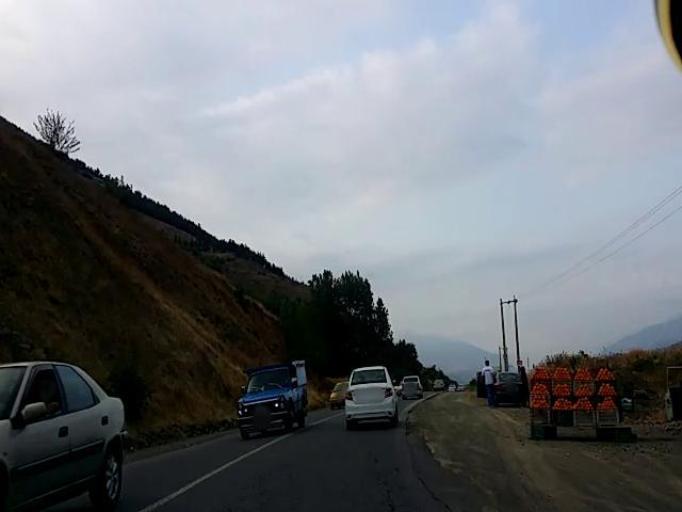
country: IR
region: Mazandaran
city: Chalus
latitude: 36.4140
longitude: 51.2788
